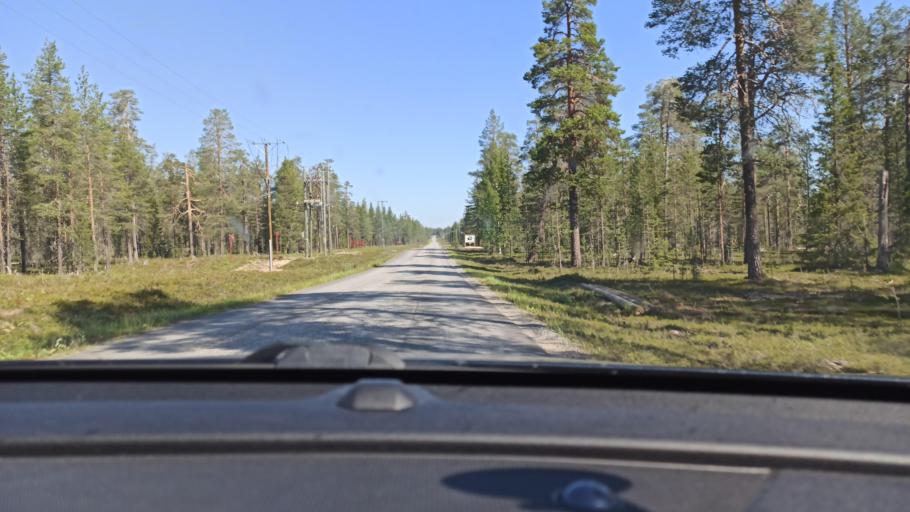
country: FI
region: Lapland
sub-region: Tunturi-Lappi
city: Kolari
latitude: 67.6444
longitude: 24.1594
